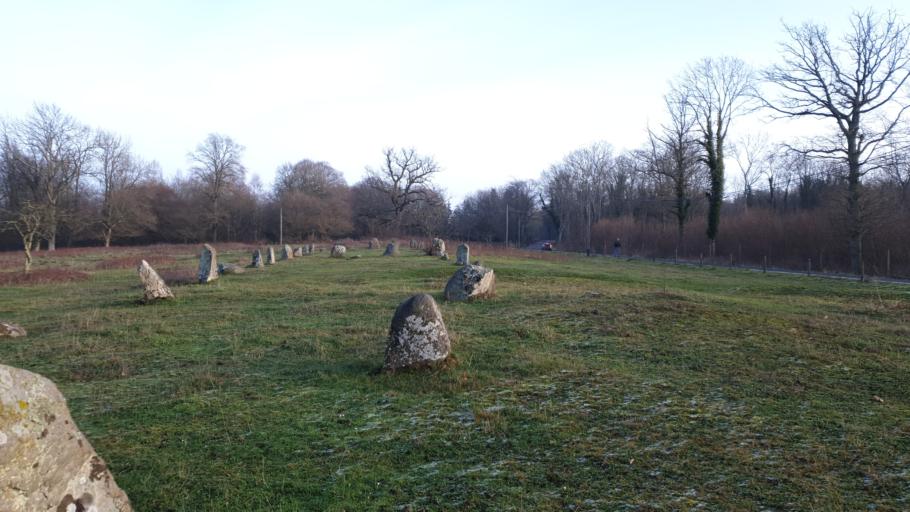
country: SE
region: Skane
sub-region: Simrishamns Kommun
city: Kivik
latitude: 55.6814
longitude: 14.2419
